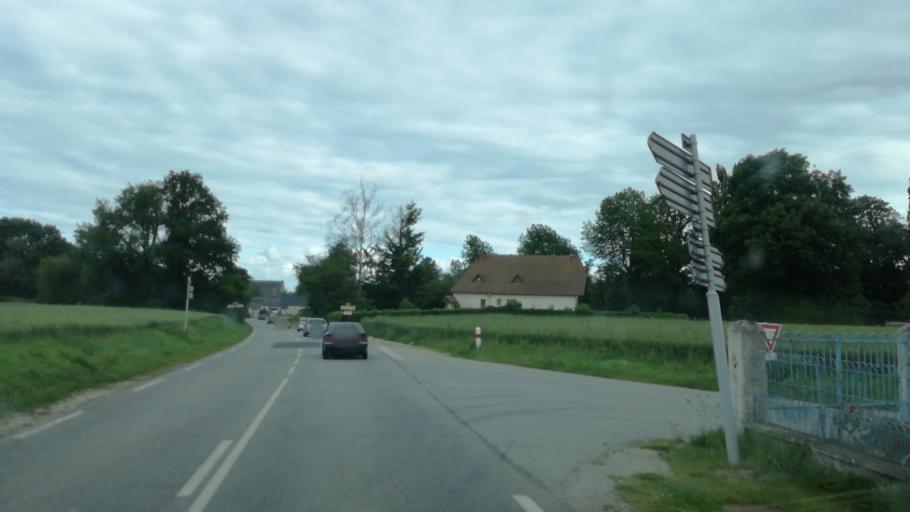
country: FR
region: Haute-Normandie
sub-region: Departement de l'Eure
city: Bourgtheroulde-Infreville
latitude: 49.2296
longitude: 0.8379
